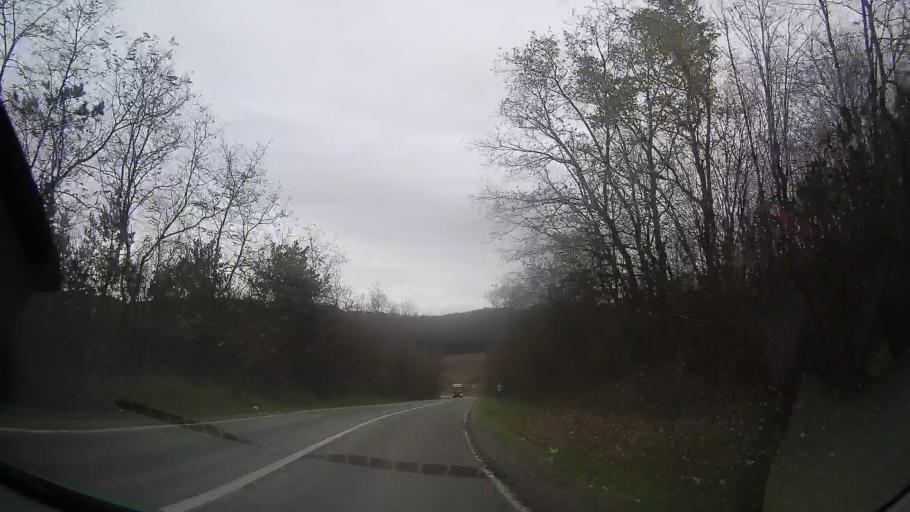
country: RO
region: Mures
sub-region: Comuna Sarmasu
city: Sarmasu
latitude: 46.7916
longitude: 24.1833
